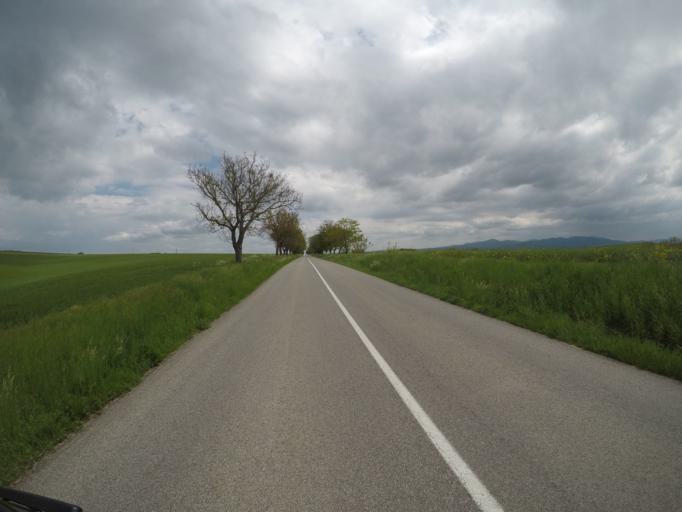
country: SK
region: Banskobystricky
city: Dudince
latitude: 48.0812
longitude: 18.8091
